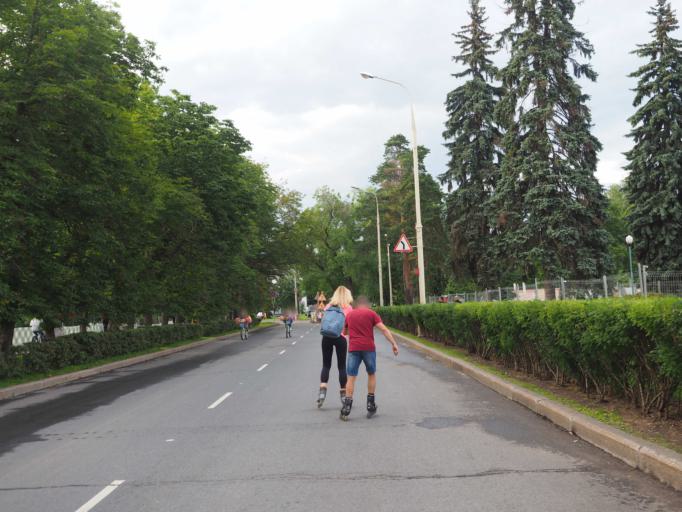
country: RU
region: Moscow
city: Sviblovo
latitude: 55.8314
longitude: 37.6354
